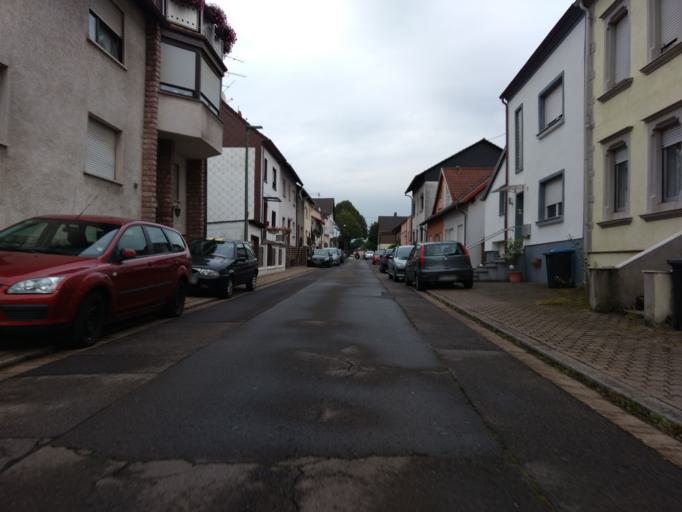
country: DE
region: Saarland
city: Nalbach
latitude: 49.3701
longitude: 6.7612
